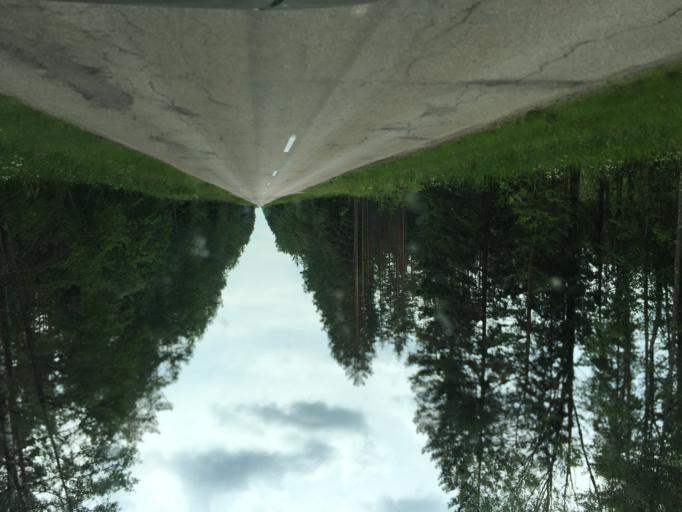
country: LV
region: Rugaju
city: Rugaji
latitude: 56.7854
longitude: 27.1027
